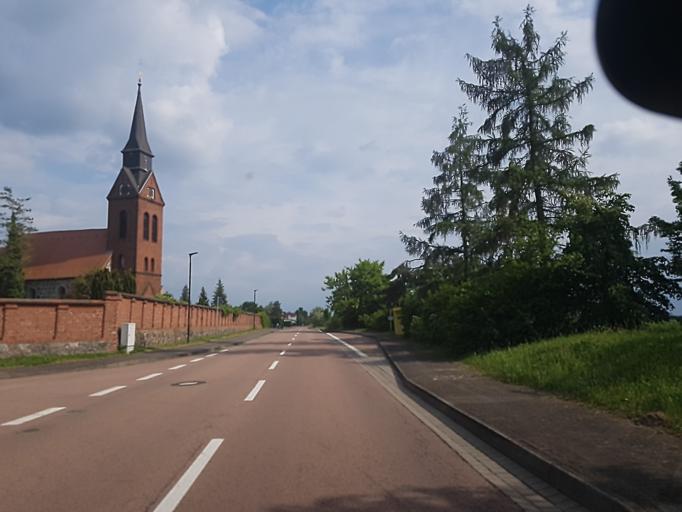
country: DE
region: Saxony-Anhalt
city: Klieken
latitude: 51.9132
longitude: 12.4105
